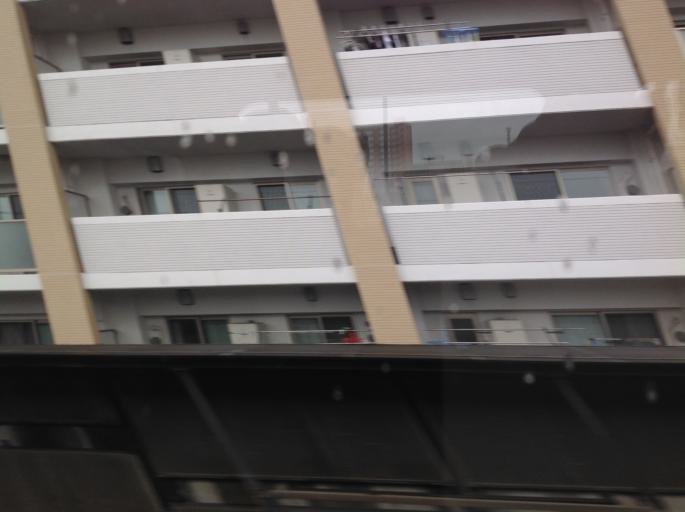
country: JP
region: Miyagi
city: Sendai
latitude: 38.2211
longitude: 140.8838
